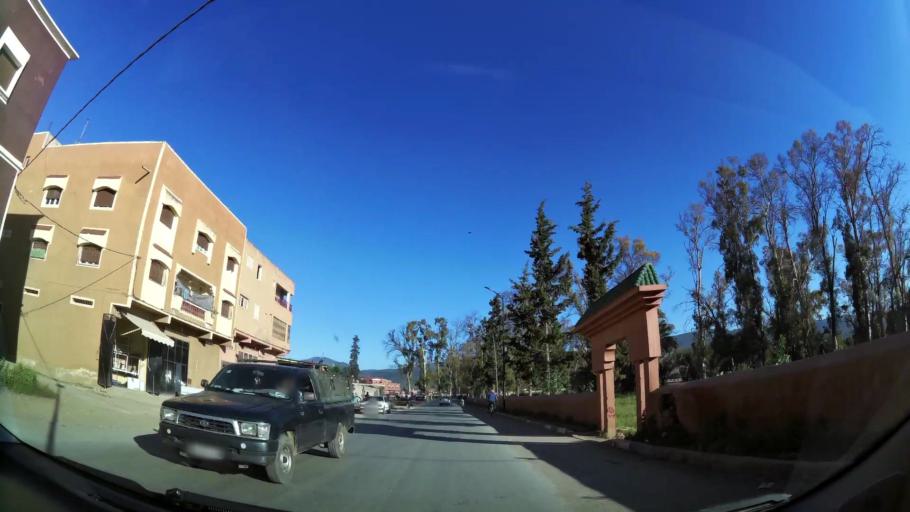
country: MA
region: Oriental
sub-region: Berkane-Taourirt
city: Berkane
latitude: 34.9237
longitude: -2.3399
